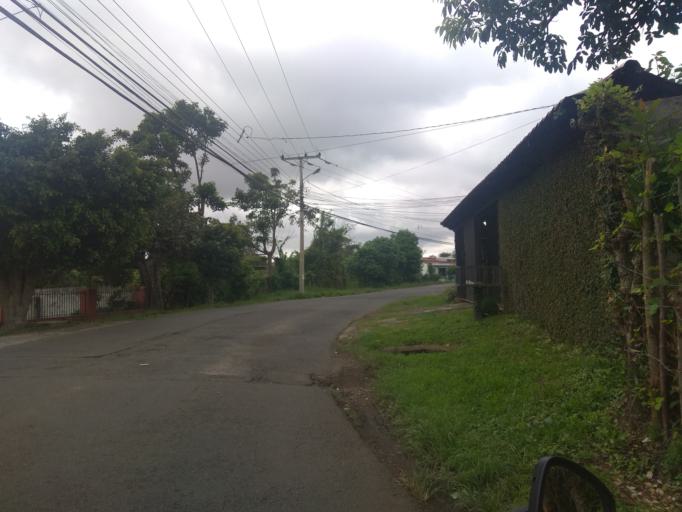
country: CR
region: Heredia
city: San Josecito
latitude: 10.0219
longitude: -84.1059
